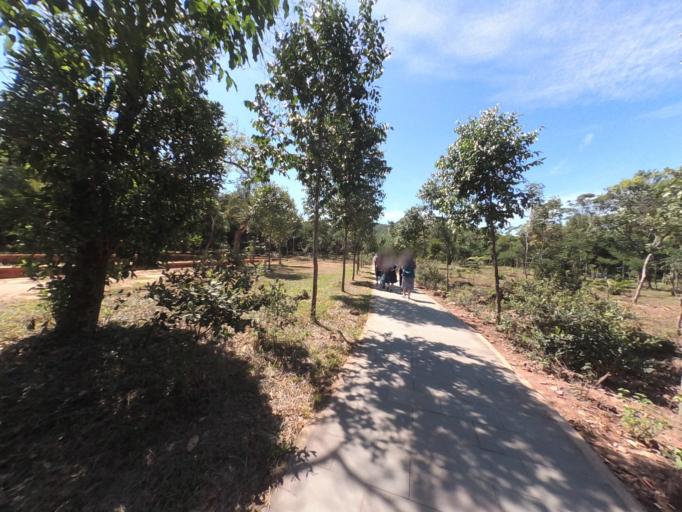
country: VN
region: Quang Nam
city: Dai Loc
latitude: 15.7677
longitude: 108.1210
